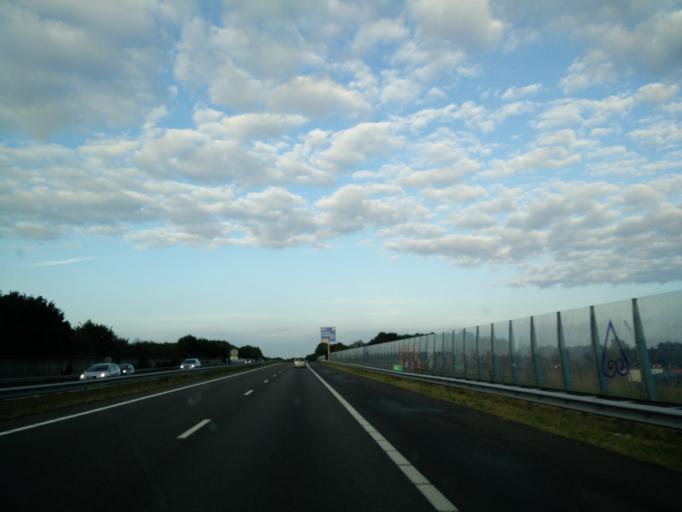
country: NL
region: Gelderland
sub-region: Gemeente Harderwijk
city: Harderwijk
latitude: 52.3312
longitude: 5.6069
